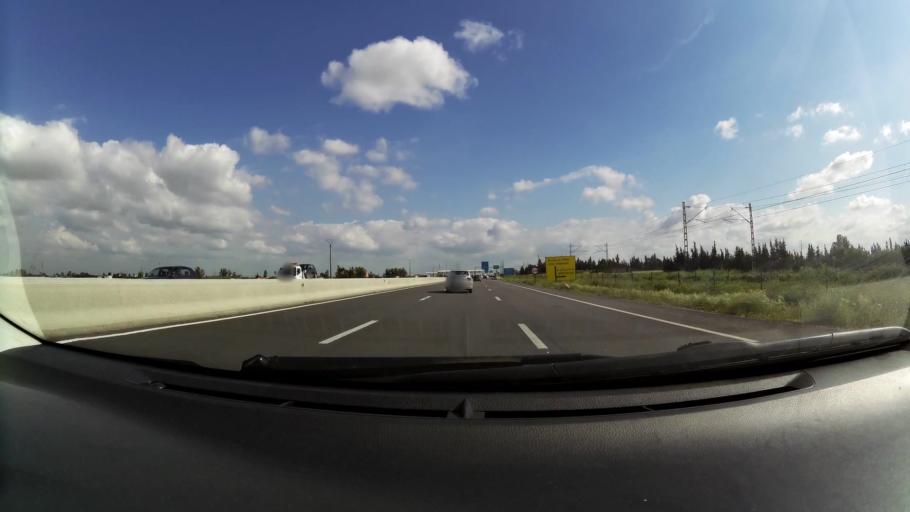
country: MA
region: Chaouia-Ouardigha
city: Nouaseur
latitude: 33.3268
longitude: -7.6071
